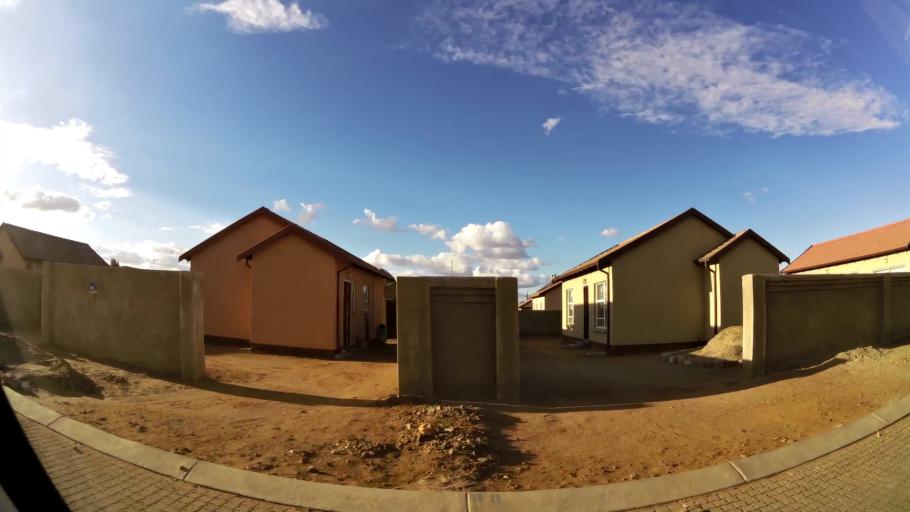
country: ZA
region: Limpopo
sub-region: Capricorn District Municipality
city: Polokwane
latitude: -23.9213
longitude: 29.4206
